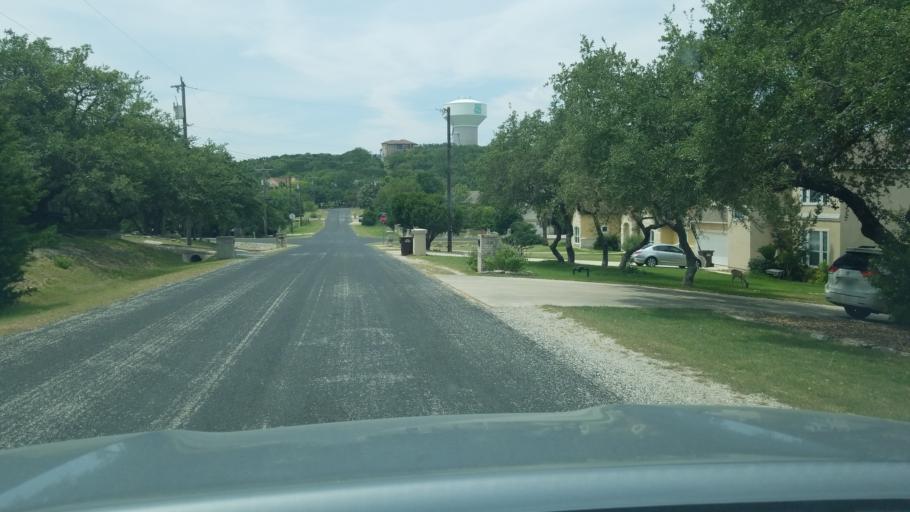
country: US
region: Texas
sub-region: Bexar County
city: Timberwood Park
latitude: 29.6853
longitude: -98.5090
